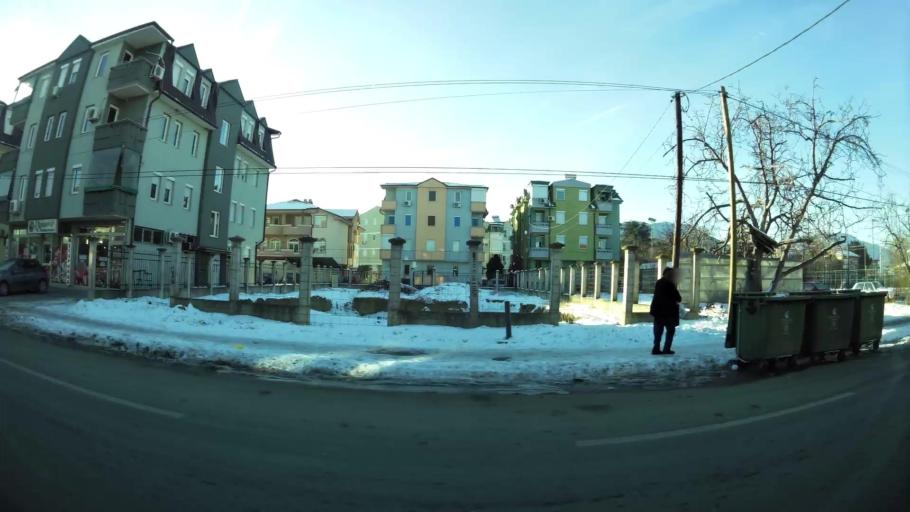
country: MK
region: Saraj
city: Saraj
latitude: 42.0089
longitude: 21.3517
